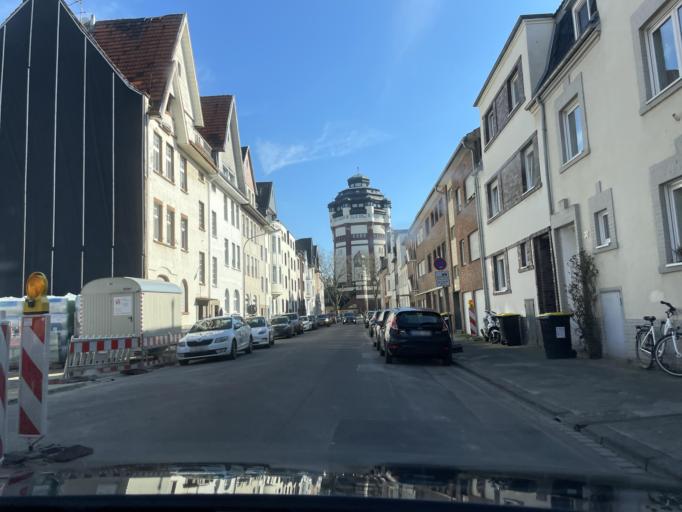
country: DE
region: North Rhine-Westphalia
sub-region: Regierungsbezirk Dusseldorf
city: Monchengladbach
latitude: 51.2023
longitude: 6.4247
